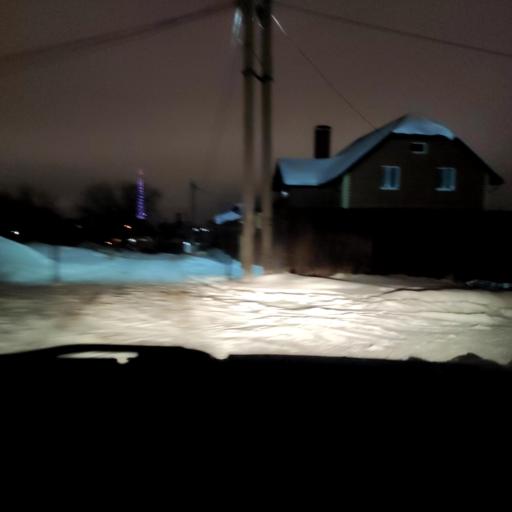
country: RU
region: Perm
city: Perm
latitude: 58.0186
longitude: 56.3256
